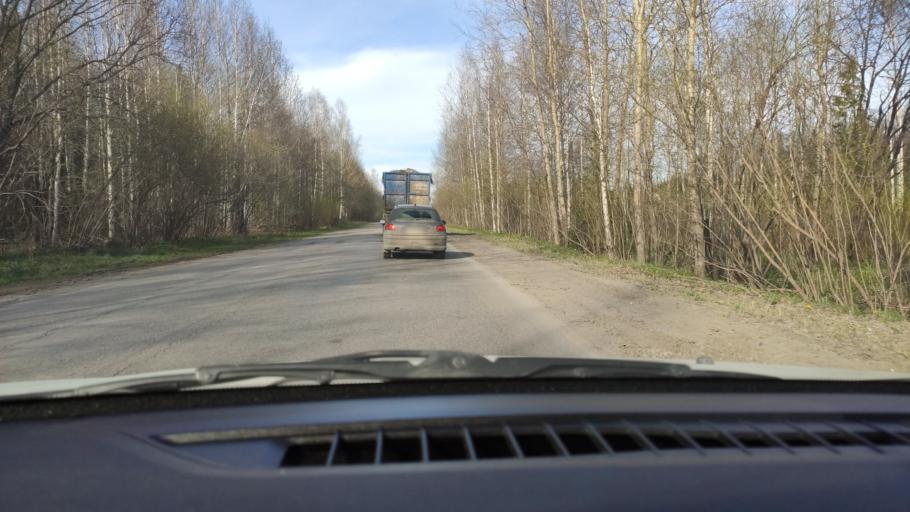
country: RU
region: Perm
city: Novyye Lyady
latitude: 57.9356
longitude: 56.4840
